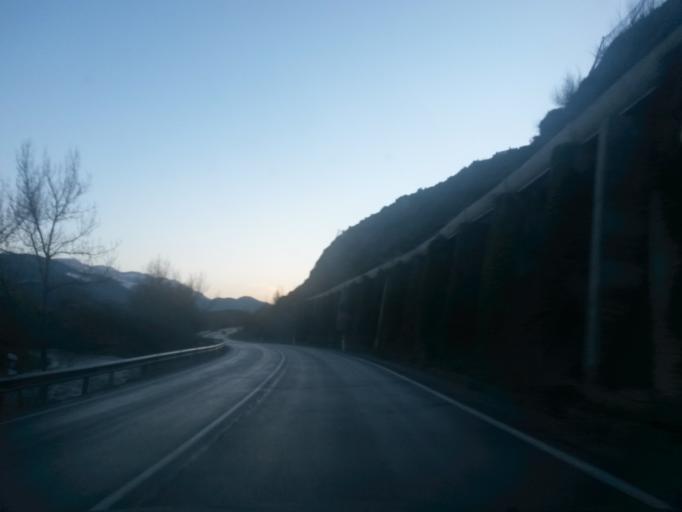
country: ES
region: Catalonia
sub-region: Provincia de Lleida
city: Bellver de Cerdanya
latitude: 42.3744
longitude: 1.7697
